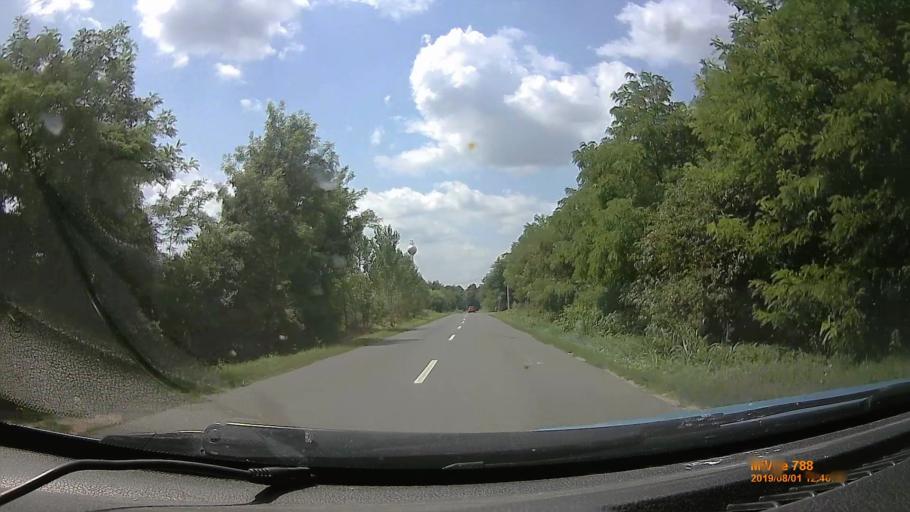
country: HU
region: Baranya
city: Harkany
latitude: 45.8370
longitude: 18.1896
